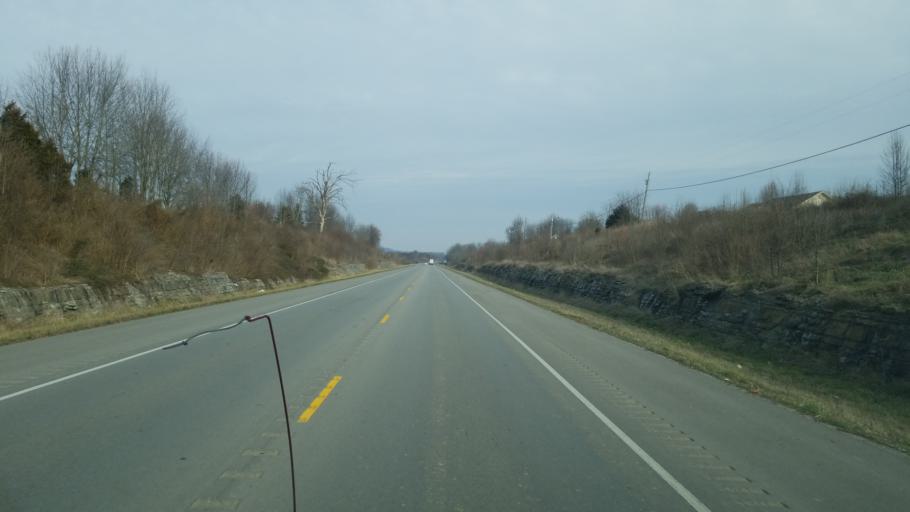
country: US
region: Kentucky
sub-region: Boyle County
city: Junction City
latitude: 37.5232
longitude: -84.8058
